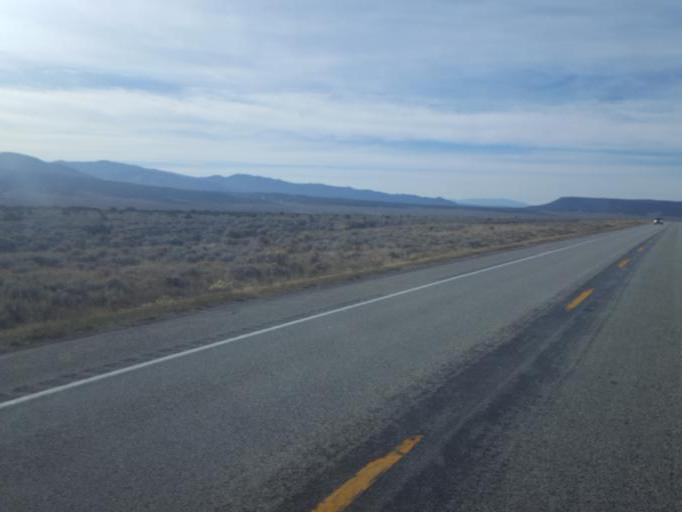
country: US
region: Colorado
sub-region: Costilla County
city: San Luis
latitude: 37.4719
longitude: -105.3506
